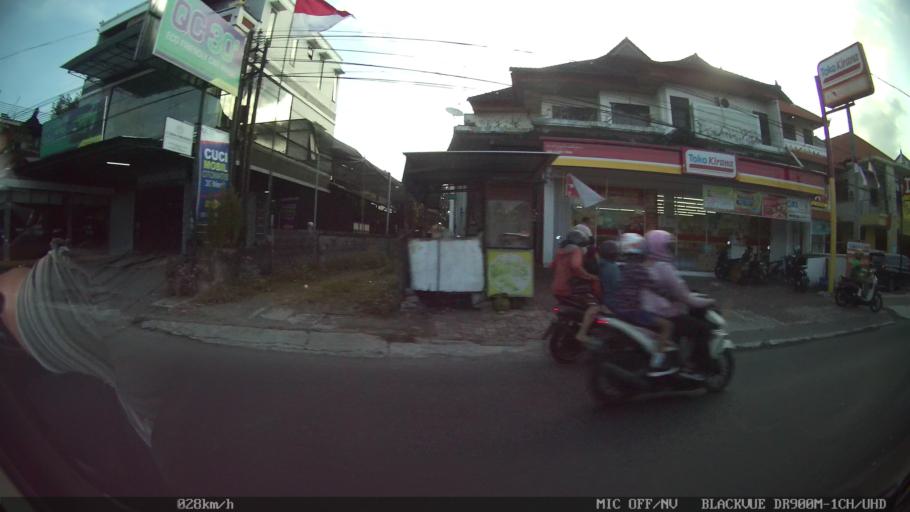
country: ID
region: Bali
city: Banjar Kertasari
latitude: -8.6271
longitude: 115.2079
